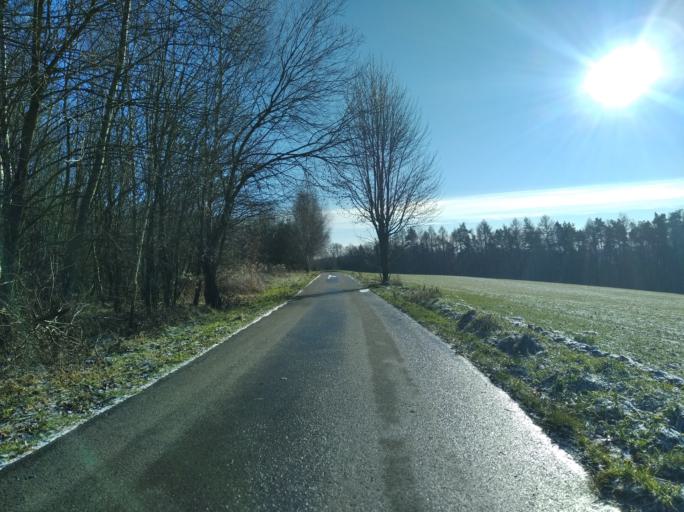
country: PL
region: Subcarpathian Voivodeship
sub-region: Powiat ropczycko-sedziszowski
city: Iwierzyce
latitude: 49.9611
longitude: 21.7514
